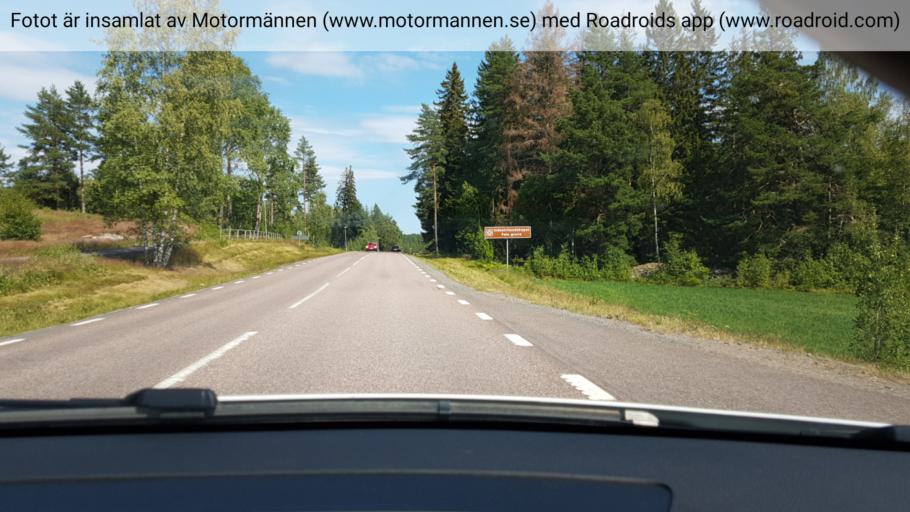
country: SE
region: Dalarna
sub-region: Borlange Kommun
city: Ornas
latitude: 60.5977
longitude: 15.5332
